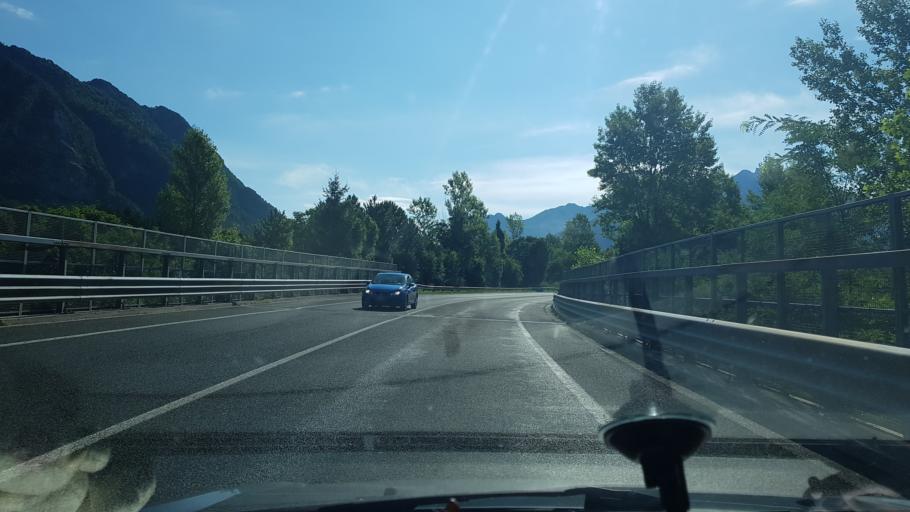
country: IT
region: Friuli Venezia Giulia
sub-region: Provincia di Udine
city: Amaro
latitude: 46.3730
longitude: 13.0773
